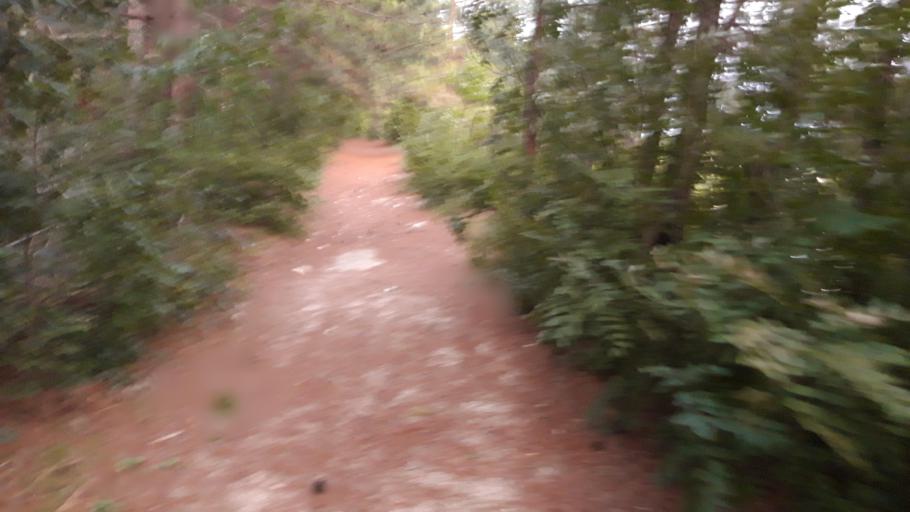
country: RU
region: Krasnodarskiy
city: Gelendzhik
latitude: 44.5801
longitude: 38.0842
